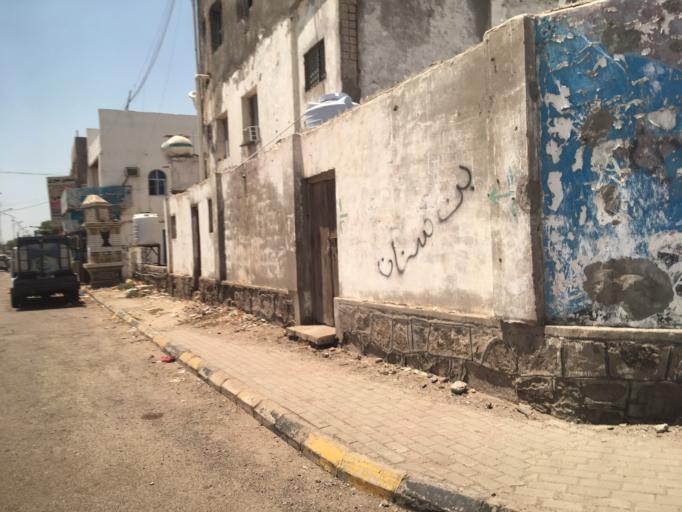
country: YE
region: Aden
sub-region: Khur Maksar
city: Khawr Maksar
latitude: 12.8075
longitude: 45.0400
